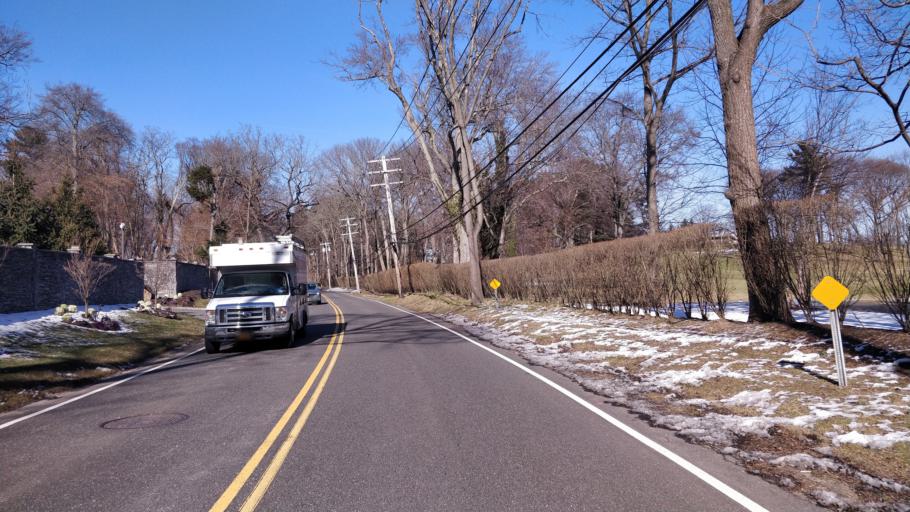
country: US
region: New York
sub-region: Nassau County
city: Old Westbury
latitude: 40.7877
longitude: -73.5878
